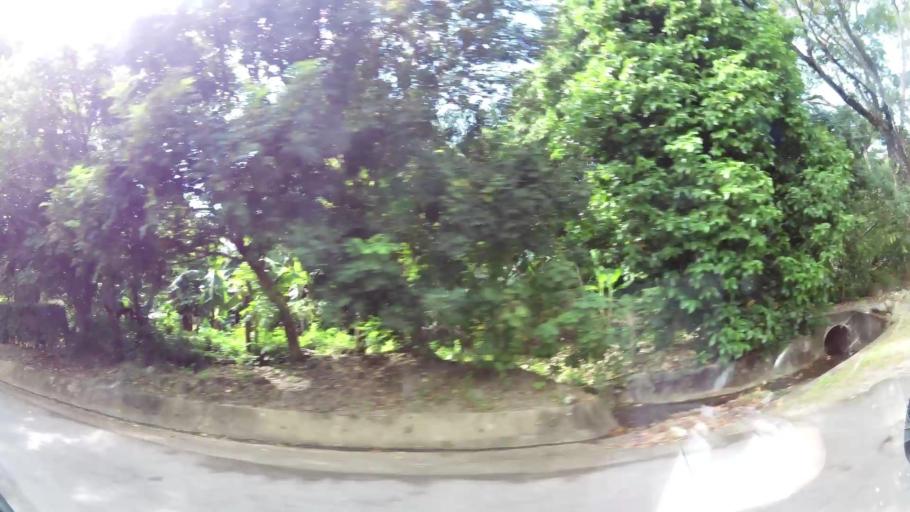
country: CR
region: Guanacaste
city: Juntas
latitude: 10.2811
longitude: -84.9479
